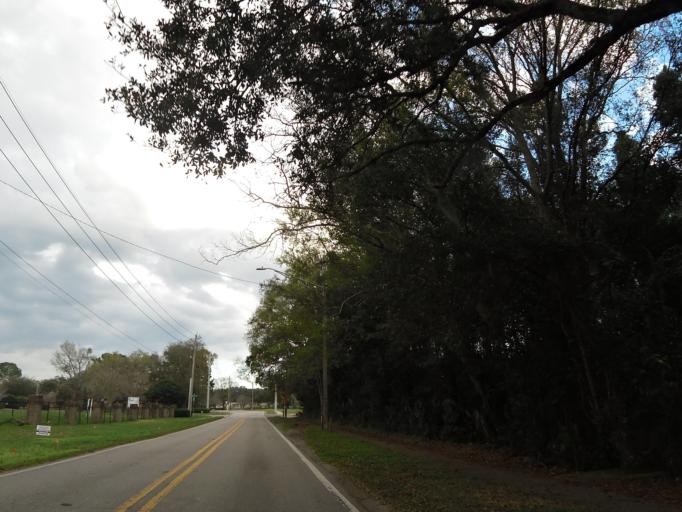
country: US
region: Florida
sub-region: Duval County
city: Jacksonville
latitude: 30.2554
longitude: -81.6240
